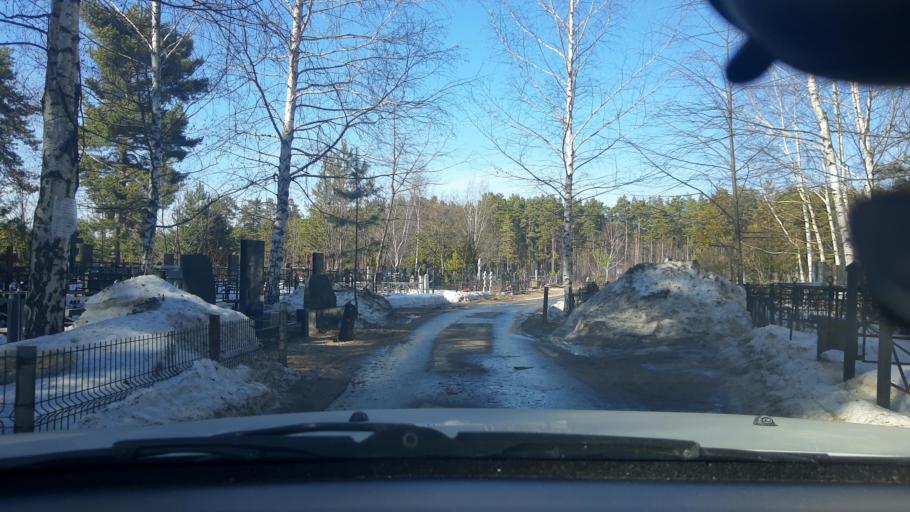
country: RU
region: Nizjnij Novgorod
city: Pyra
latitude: 56.2427
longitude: 43.3705
